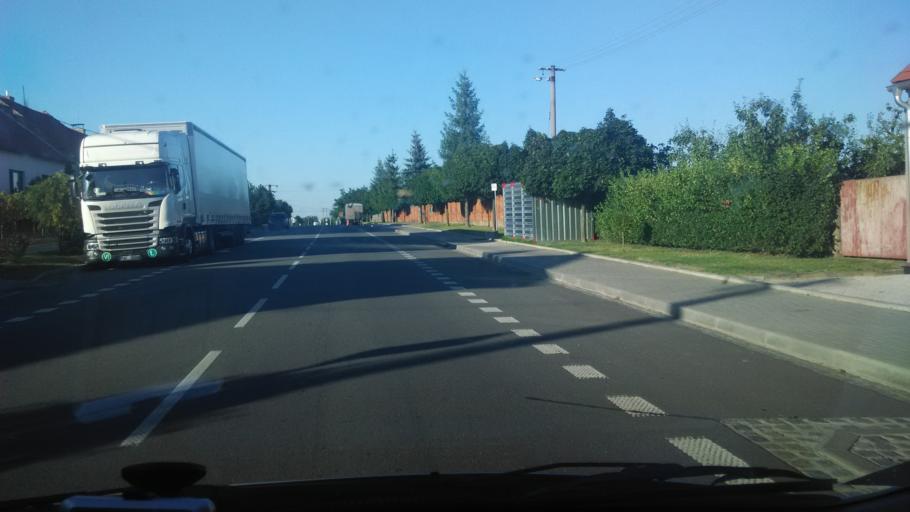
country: CZ
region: South Moravian
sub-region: Okres Breclav
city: Lanzhot
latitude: 48.7273
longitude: 16.9712
